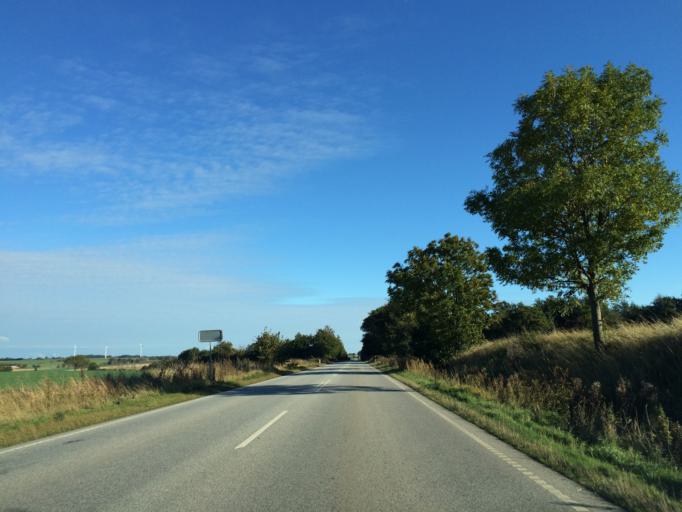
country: DK
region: Central Jutland
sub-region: Randers Kommune
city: Randers
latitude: 56.4055
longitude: 10.0000
